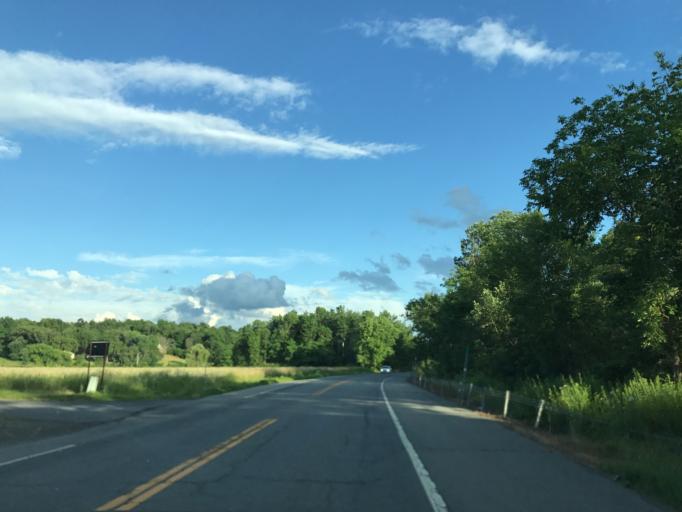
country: US
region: New York
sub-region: Saratoga County
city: Schuylerville
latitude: 43.1599
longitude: -73.5772
